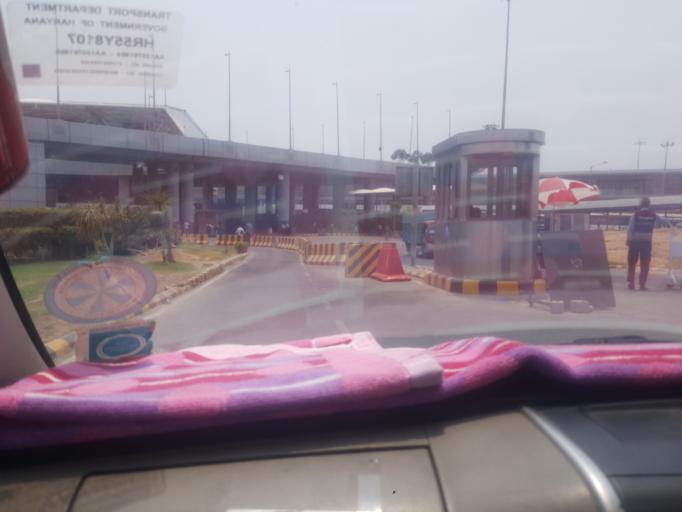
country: IN
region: Haryana
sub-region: Gurgaon
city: Gurgaon
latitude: 28.5573
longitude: 77.0856
